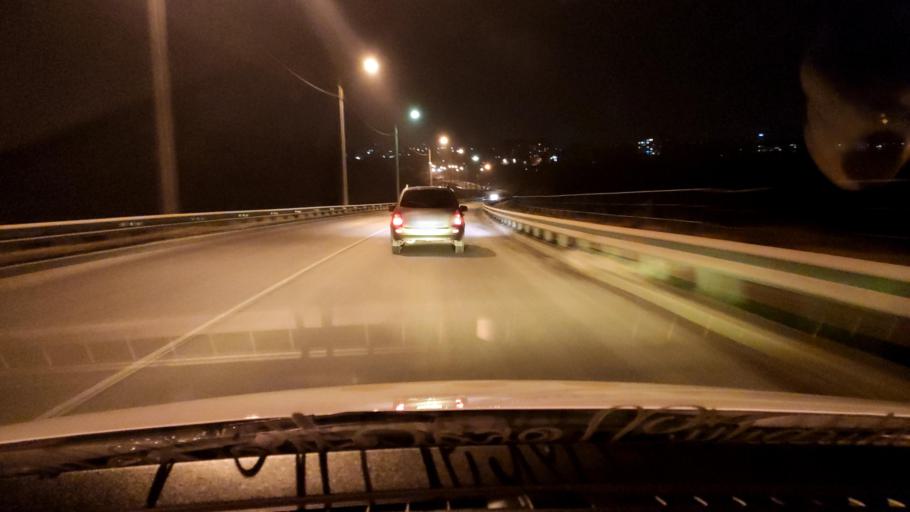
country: RU
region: Voronezj
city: Semiluki
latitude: 51.6711
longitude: 39.0358
